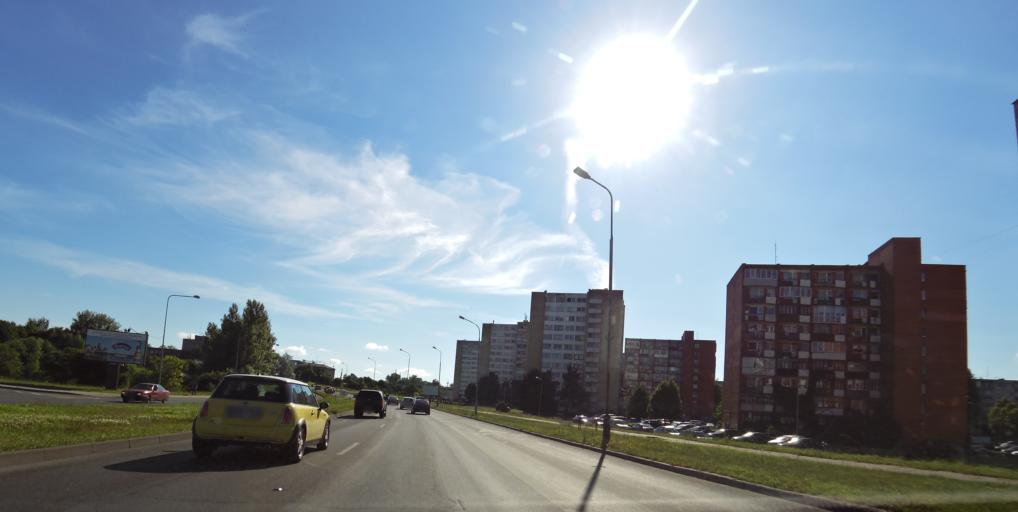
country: LT
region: Vilnius County
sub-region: Vilnius
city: Vilnius
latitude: 54.7133
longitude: 25.2799
